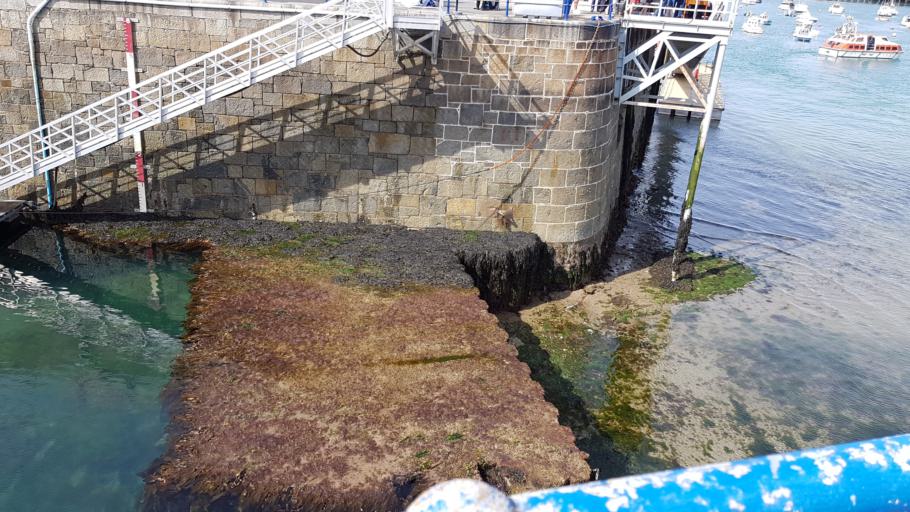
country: GG
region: St Peter Port
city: Saint Peter Port
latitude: 49.4539
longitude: -2.5334
